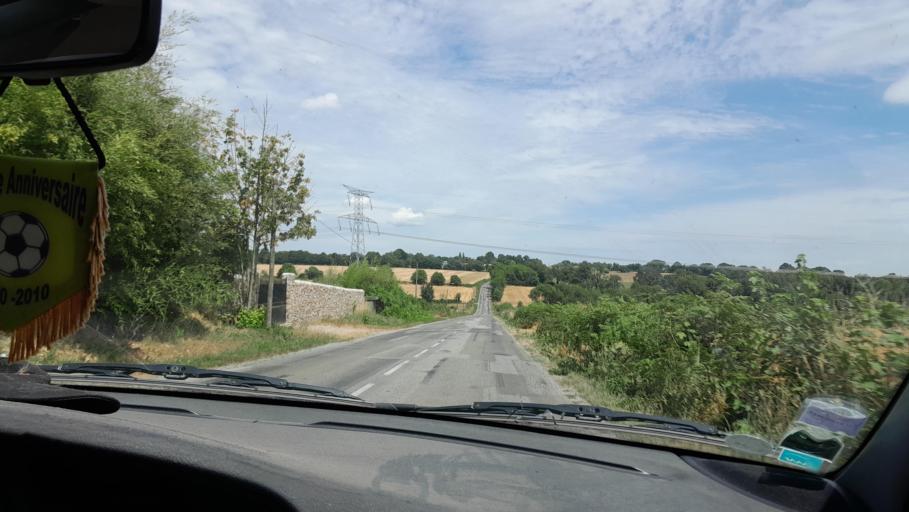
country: FR
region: Brittany
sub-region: Departement d'Ille-et-Vilaine
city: Le Pertre
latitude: 48.0581
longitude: -1.0313
